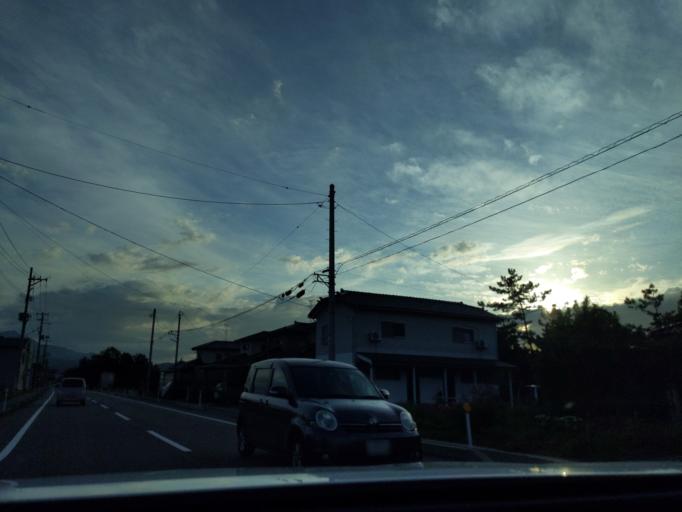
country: JP
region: Niigata
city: Kashiwazaki
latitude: 37.3811
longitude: 138.5597
